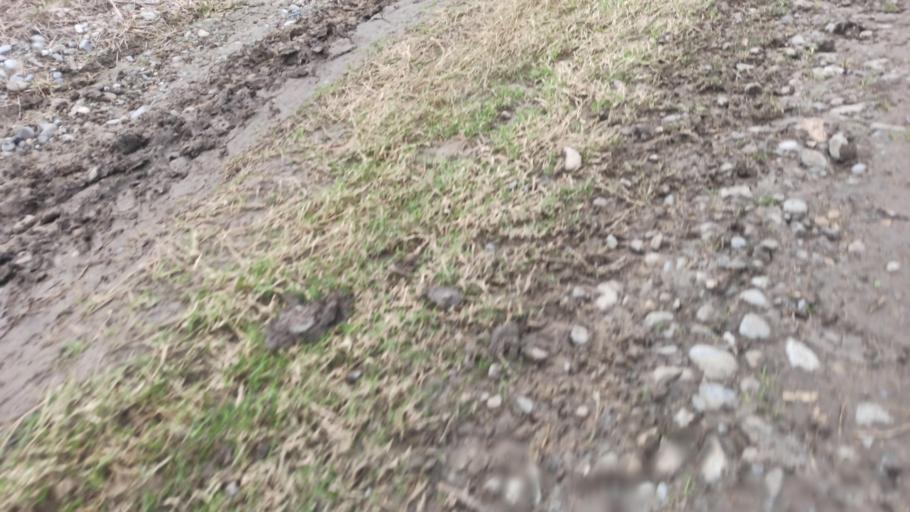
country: MX
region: Puebla
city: Espinal
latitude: 20.3017
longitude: -97.4099
